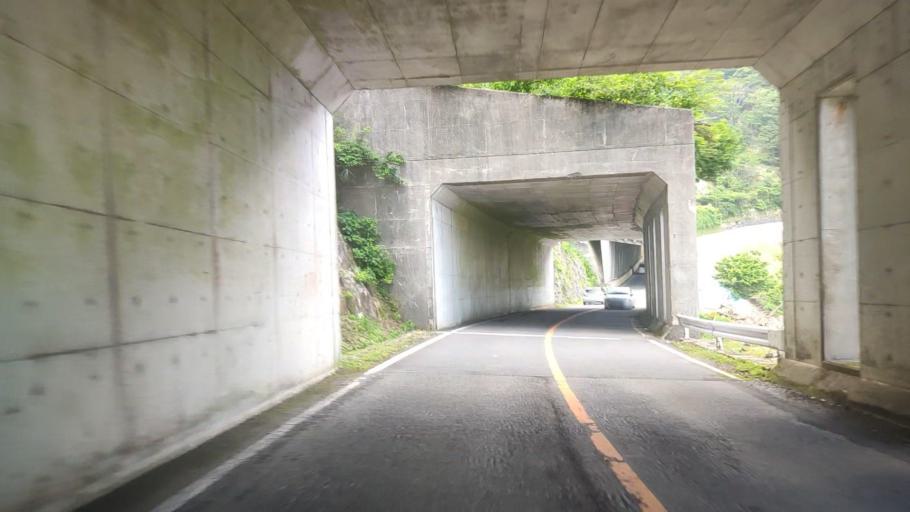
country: JP
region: Gifu
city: Tarui
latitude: 35.4210
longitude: 136.4173
